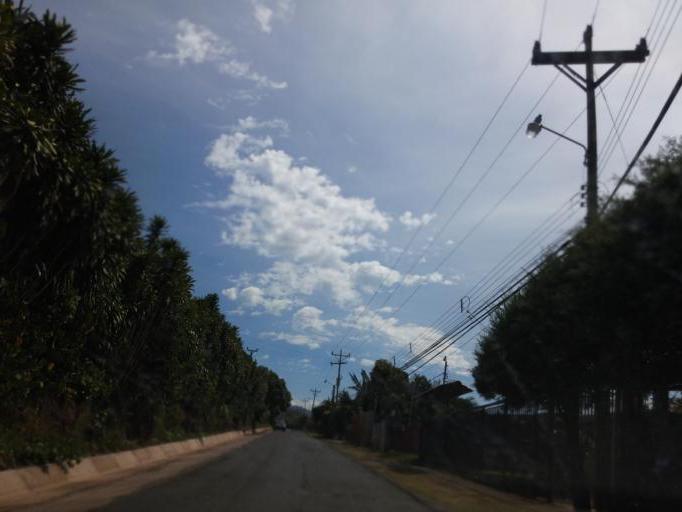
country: CR
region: Alajuela
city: Sabanilla
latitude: 10.0445
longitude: -84.2272
